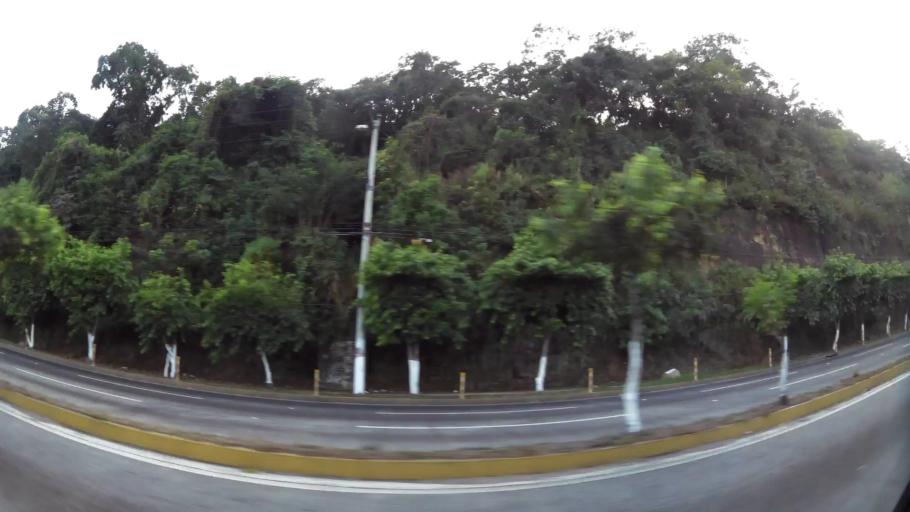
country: SV
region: San Salvador
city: San Salvador
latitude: 13.6808
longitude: -89.2147
